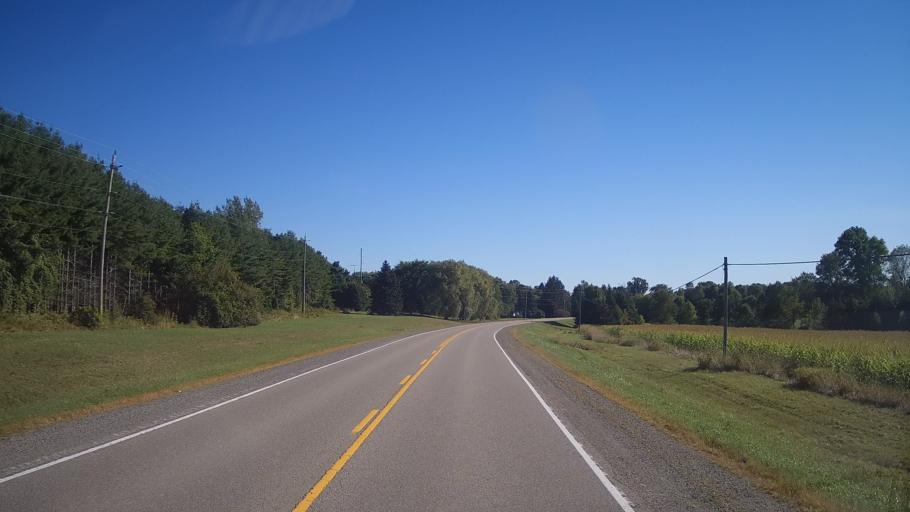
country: CA
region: Ontario
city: Gananoque
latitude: 44.6053
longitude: -76.0740
